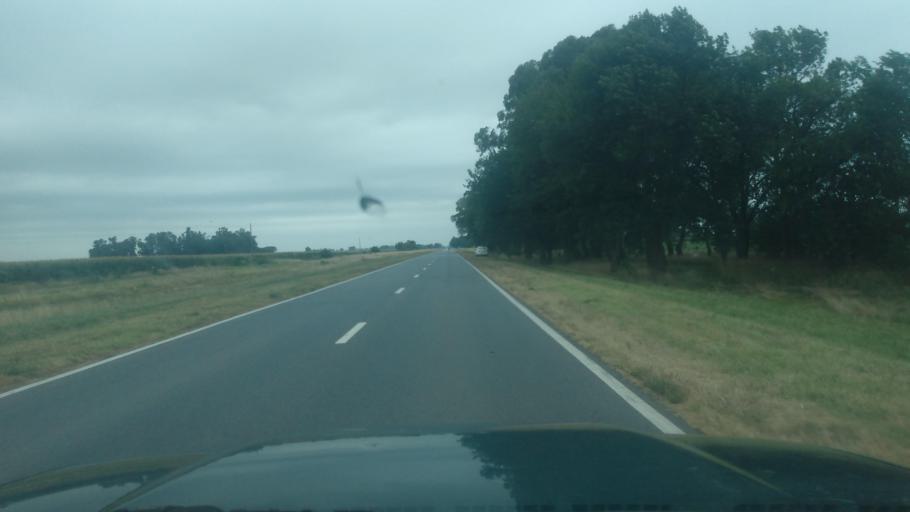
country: AR
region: Buenos Aires
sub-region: Partido de Bragado
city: Bragado
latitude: -35.3029
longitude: -60.6172
